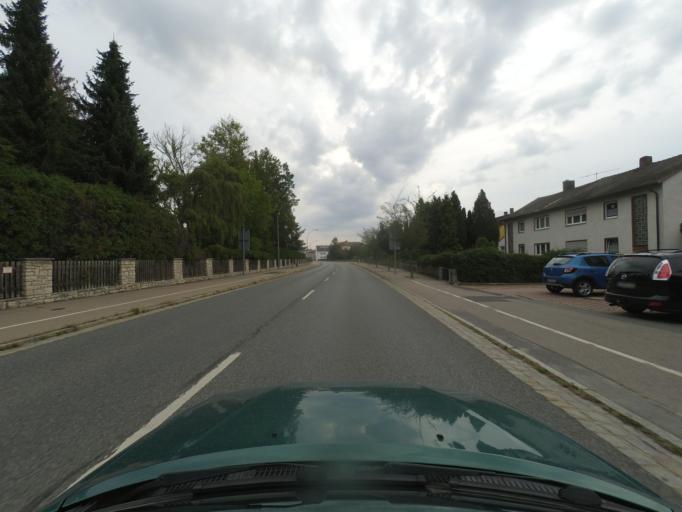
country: DE
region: Bavaria
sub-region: Upper Palatinate
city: Schnaittenbach
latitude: 49.5465
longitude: 11.9953
